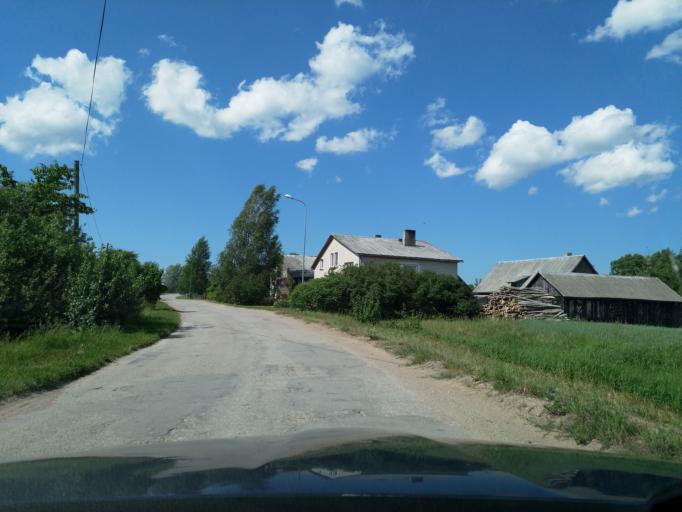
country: LV
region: Alsunga
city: Alsunga
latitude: 56.9726
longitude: 21.5683
